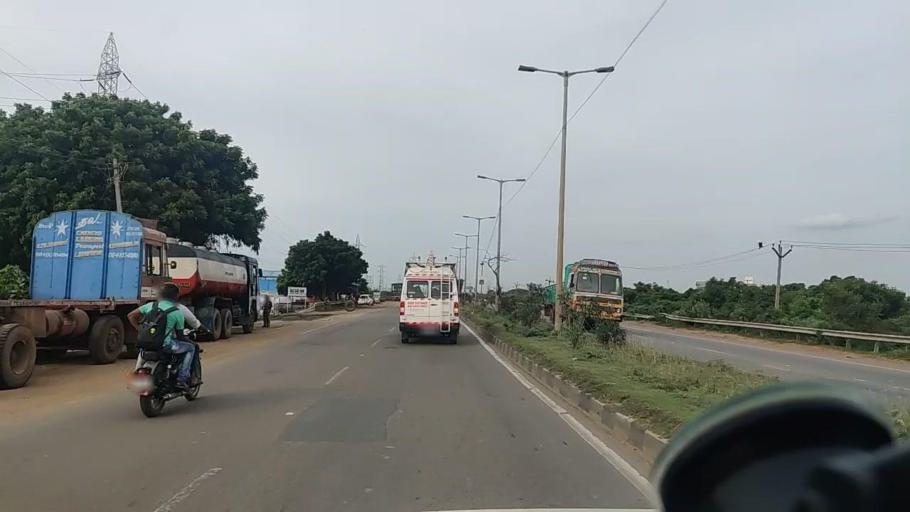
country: IN
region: Tamil Nadu
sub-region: Thiruvallur
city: Chinnasekkadu
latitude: 13.1708
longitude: 80.2328
